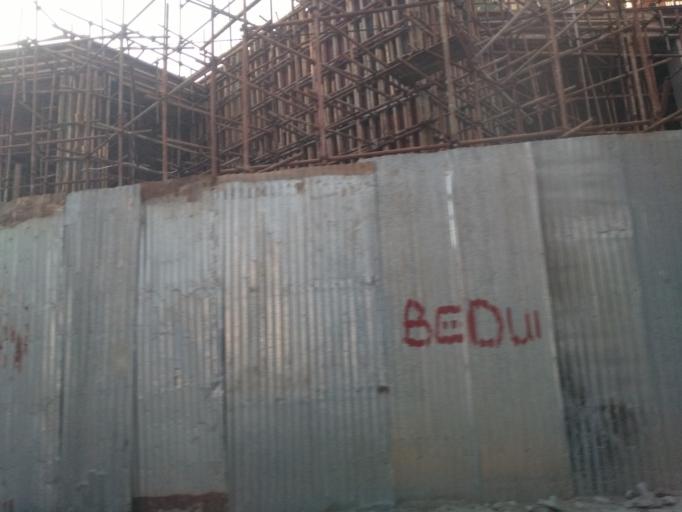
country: TZ
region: Dar es Salaam
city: Magomeni
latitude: -6.7551
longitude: 39.2472
